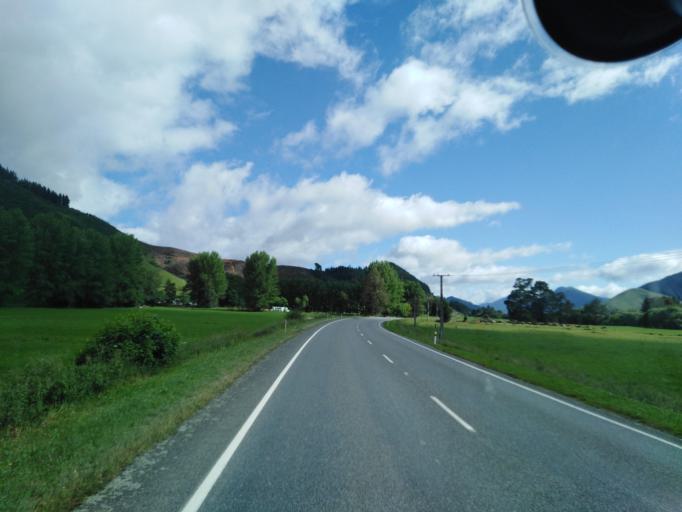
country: NZ
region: Nelson
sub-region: Nelson City
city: Nelson
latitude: -41.2685
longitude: 173.5725
